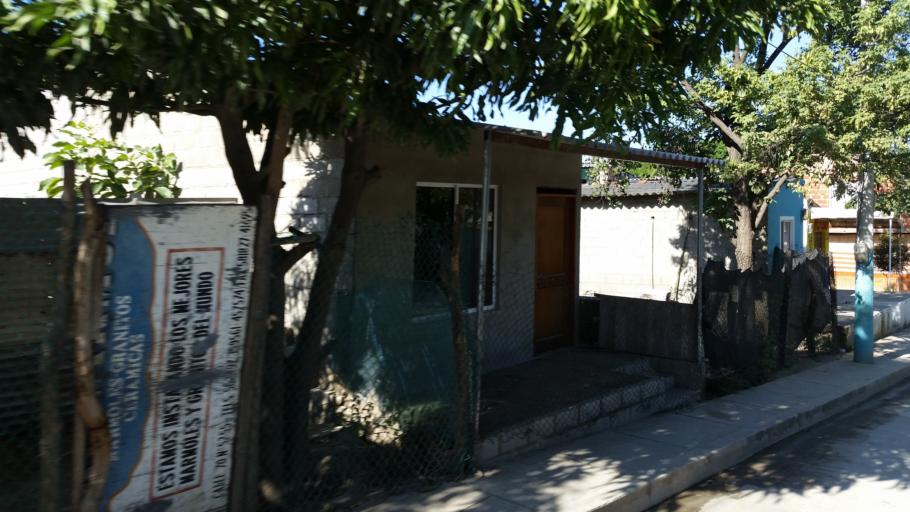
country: CO
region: Magdalena
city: Santa Marta
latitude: 11.1481
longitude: -74.2150
